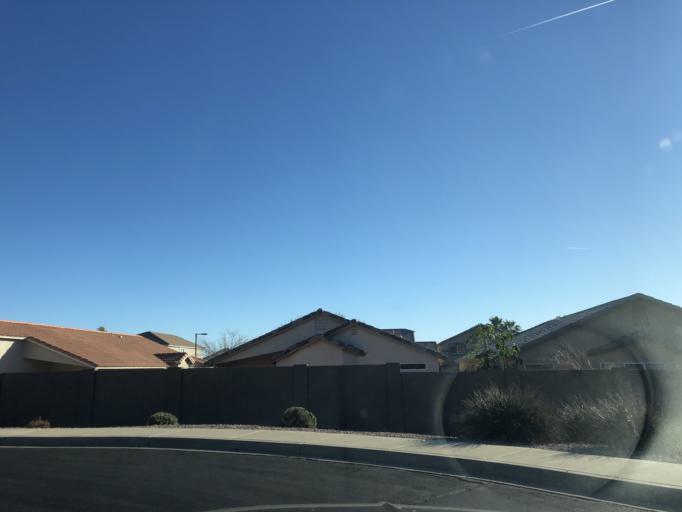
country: US
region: Arizona
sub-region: Maricopa County
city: Buckeye
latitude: 33.4393
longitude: -112.5713
